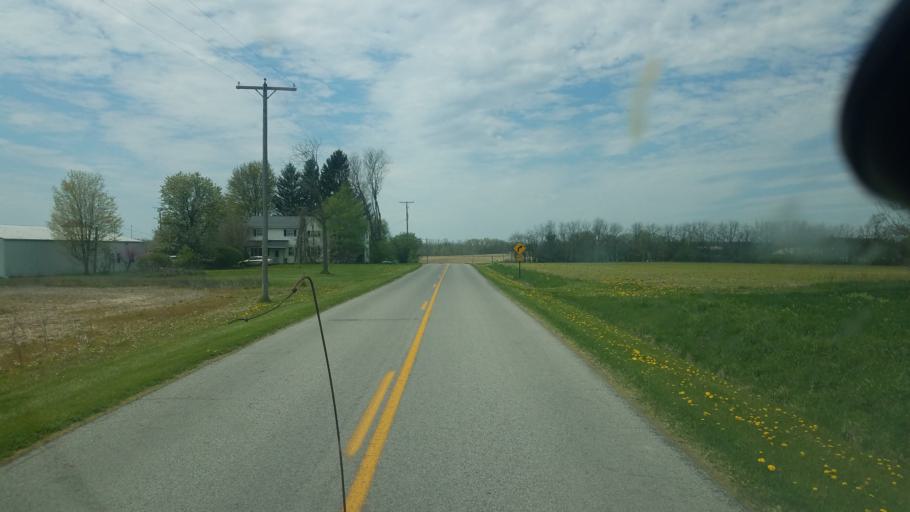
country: US
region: Ohio
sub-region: Allen County
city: Bluffton
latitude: 40.7868
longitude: -83.9446
